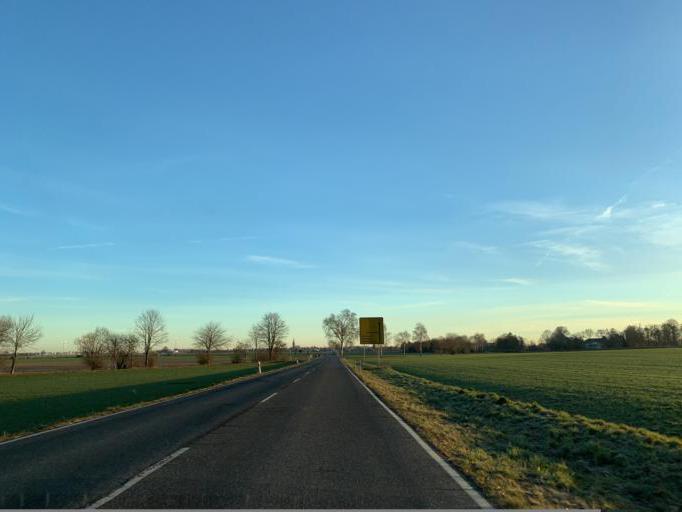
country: DE
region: North Rhine-Westphalia
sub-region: Regierungsbezirk Koln
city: Titz
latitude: 50.9900
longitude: 6.4097
